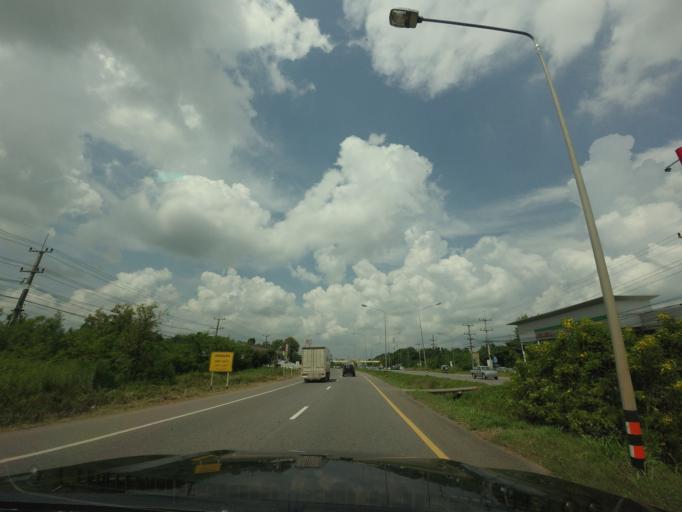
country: TH
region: Khon Kaen
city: Nong Ruea
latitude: 16.4902
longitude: 102.4462
